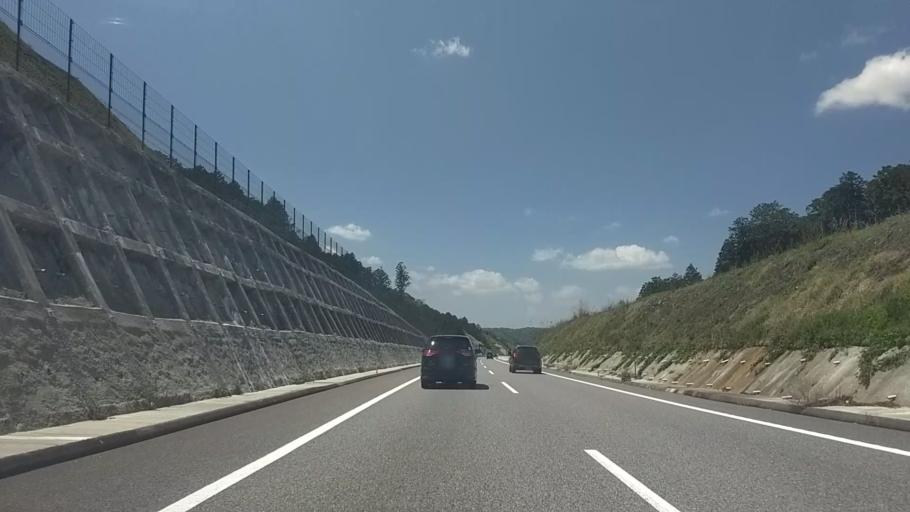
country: JP
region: Aichi
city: Gamagori
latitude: 34.9047
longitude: 137.3061
